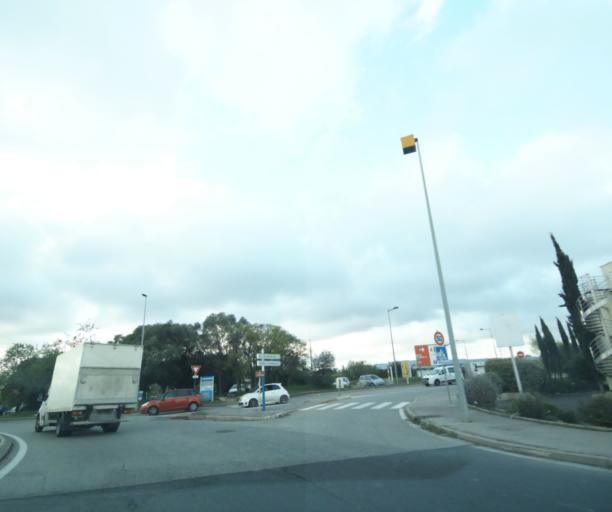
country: FR
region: Languedoc-Roussillon
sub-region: Departement de l'Herault
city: Saint-Jean-de-Vedas
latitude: 43.5702
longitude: 3.8382
